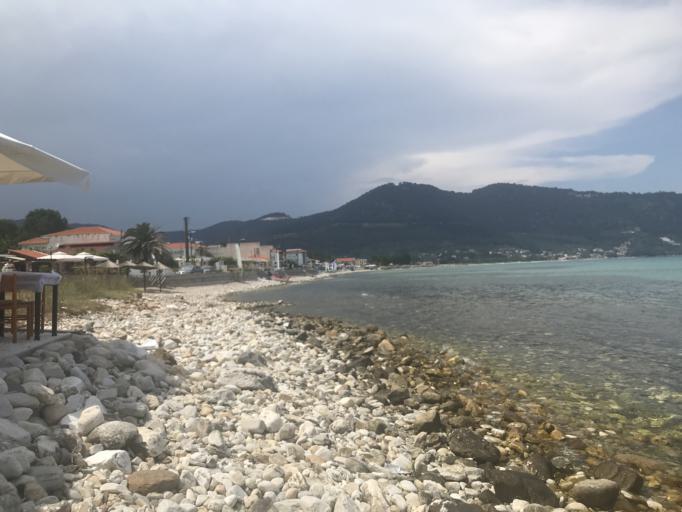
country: GR
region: East Macedonia and Thrace
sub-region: Nomos Kavalas
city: Potamia
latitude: 40.7108
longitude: 24.7593
